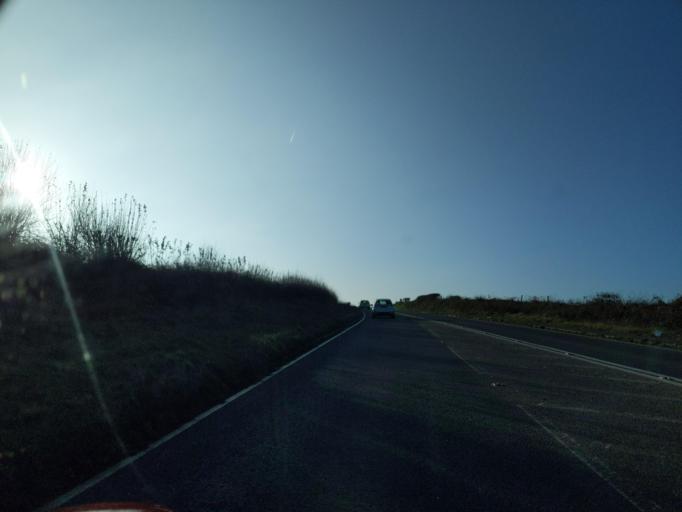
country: GB
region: England
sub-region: Cornwall
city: Liskeard
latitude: 50.4531
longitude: -4.5345
